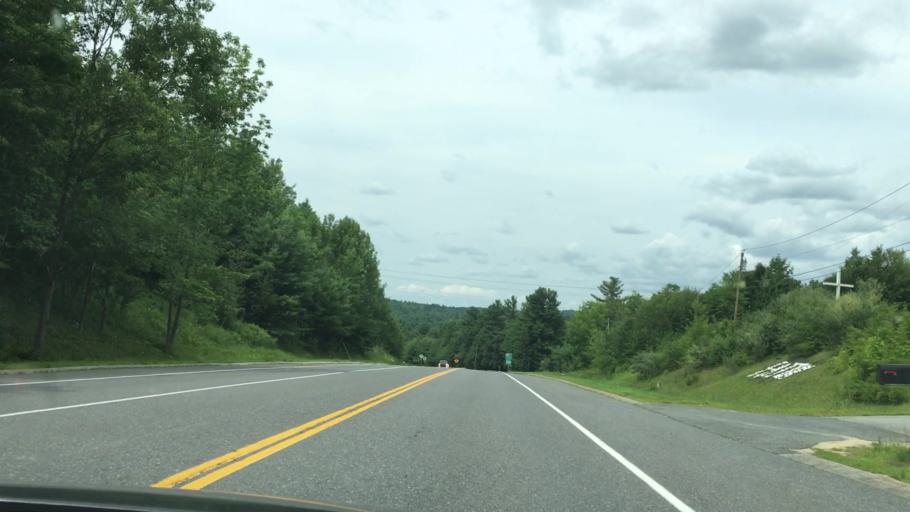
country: US
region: Massachusetts
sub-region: Worcester County
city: Gardner
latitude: 42.5994
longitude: -71.9884
